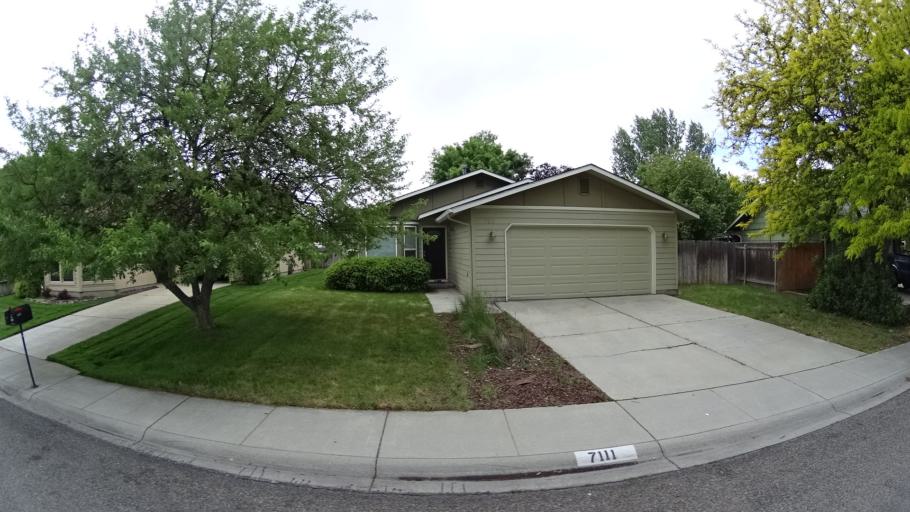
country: US
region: Idaho
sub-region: Ada County
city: Garden City
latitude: 43.6777
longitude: -116.2776
